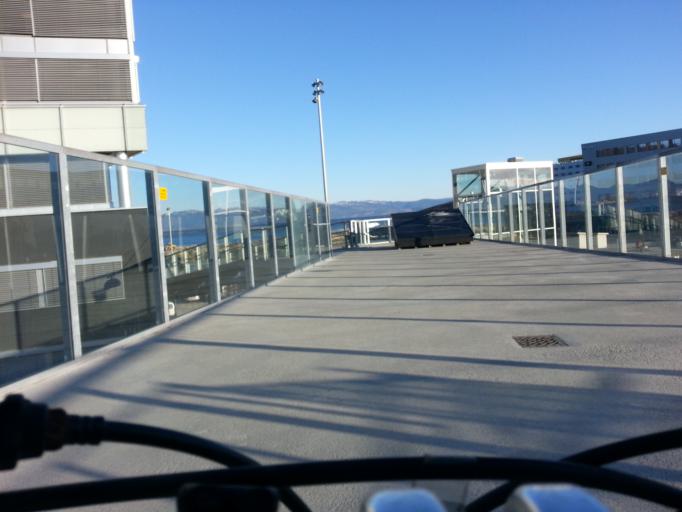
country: NO
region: Sor-Trondelag
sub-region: Trondheim
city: Trondheim
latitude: 63.4371
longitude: 10.3994
